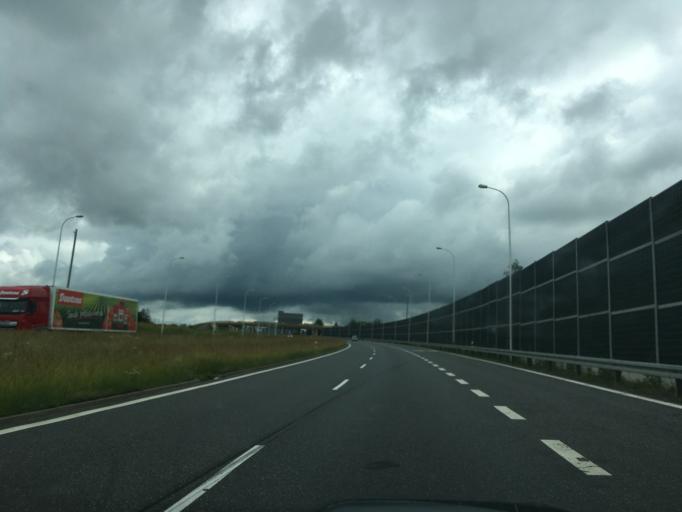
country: PL
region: Lublin Voivodeship
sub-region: Powiat swidnicki
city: Swidnik
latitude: 51.2109
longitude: 22.6552
